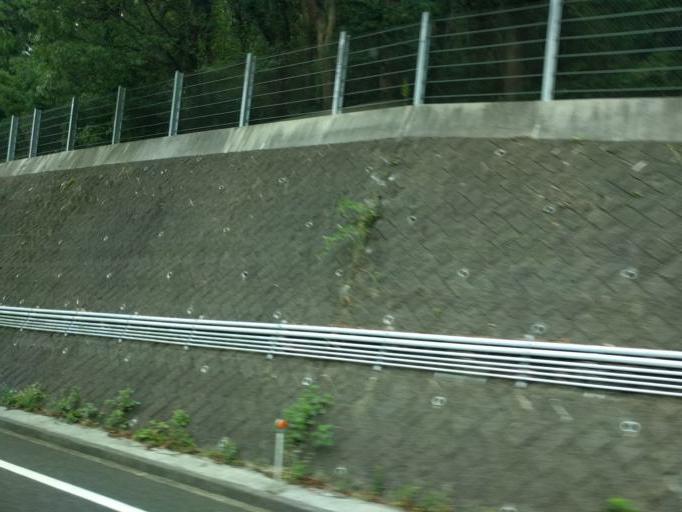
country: JP
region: Hyogo
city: Kobe
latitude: 34.6971
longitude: 135.1470
